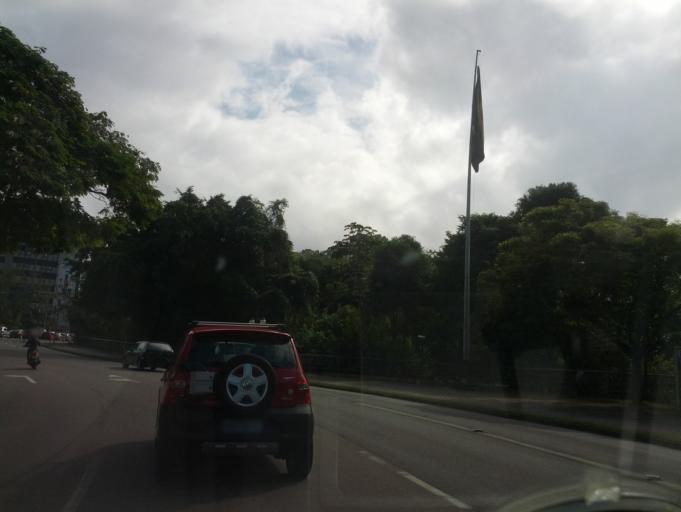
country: BR
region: Santa Catarina
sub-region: Blumenau
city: Blumenau
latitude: -26.9137
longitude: -49.0687
